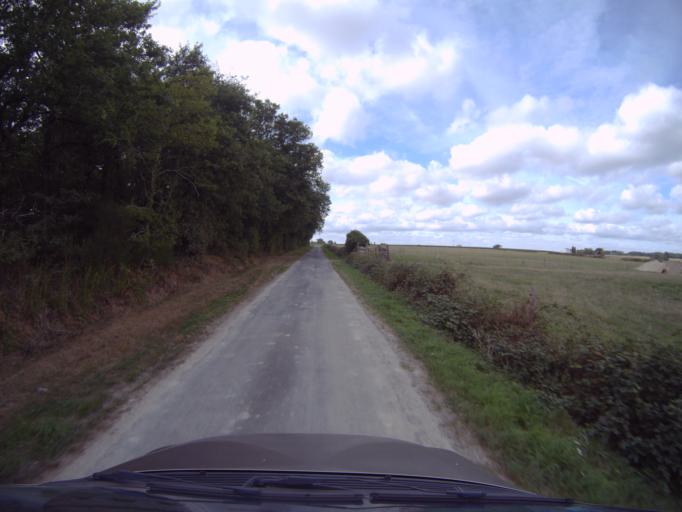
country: FR
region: Pays de la Loire
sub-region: Departement de la Loire-Atlantique
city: La Planche
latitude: 47.0311
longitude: -1.4158
